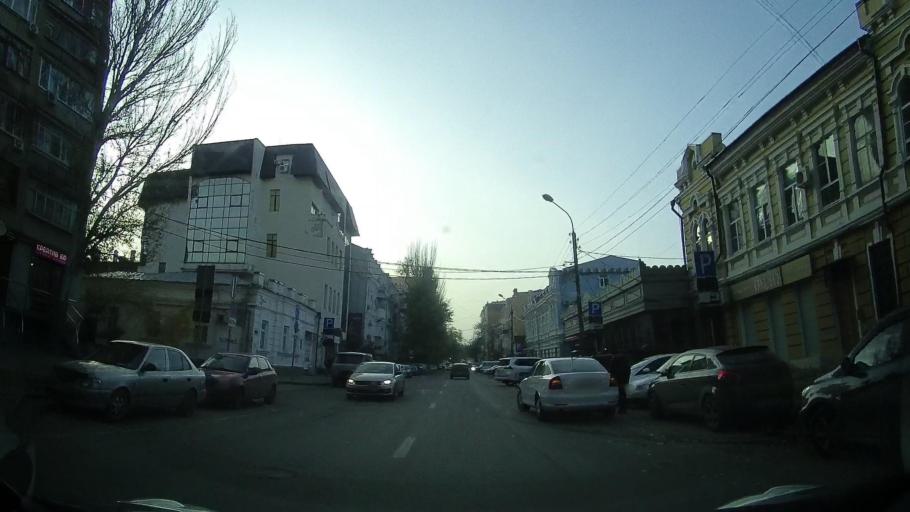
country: RU
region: Rostov
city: Rostov-na-Donu
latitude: 47.2259
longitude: 39.7230
